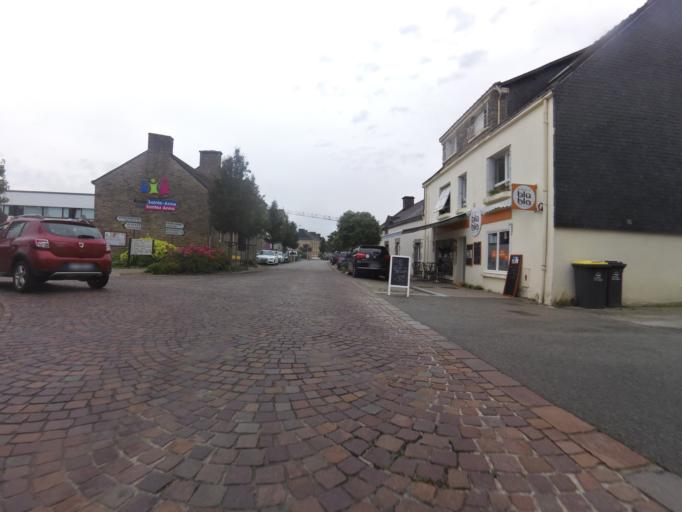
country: FR
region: Brittany
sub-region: Departement du Morbihan
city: Plescop
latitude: 47.6992
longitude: -2.8062
